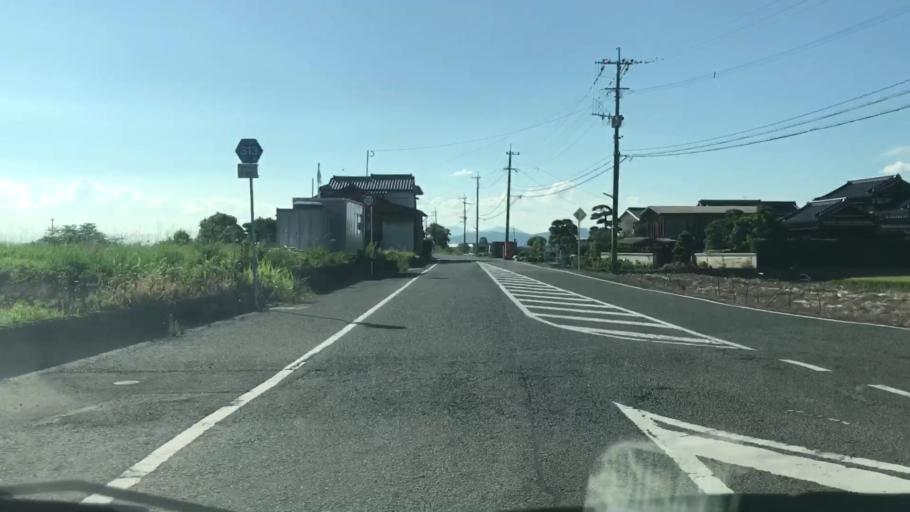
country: JP
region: Saga Prefecture
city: Saga-shi
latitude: 33.1927
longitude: 130.2783
